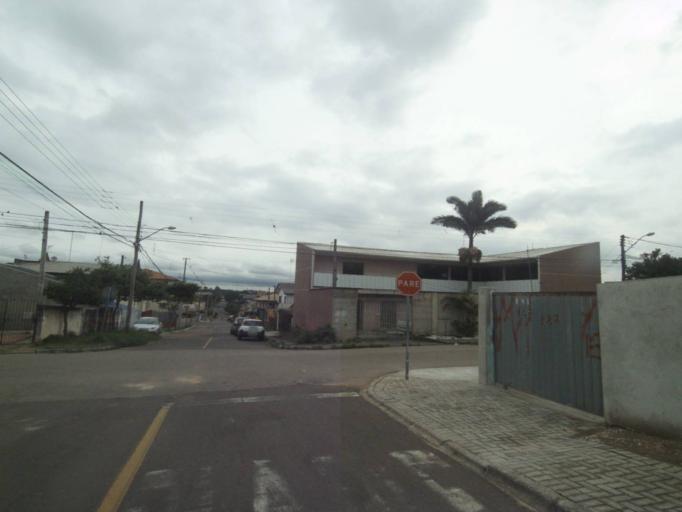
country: BR
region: Parana
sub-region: Sao Jose Dos Pinhais
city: Sao Jose dos Pinhais
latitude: -25.5503
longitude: -49.2672
